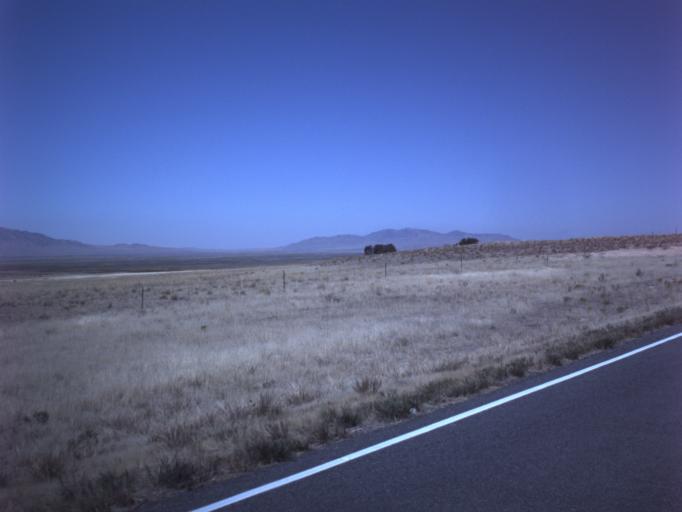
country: US
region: Utah
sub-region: Tooele County
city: Grantsville
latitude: 40.5828
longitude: -112.7245
